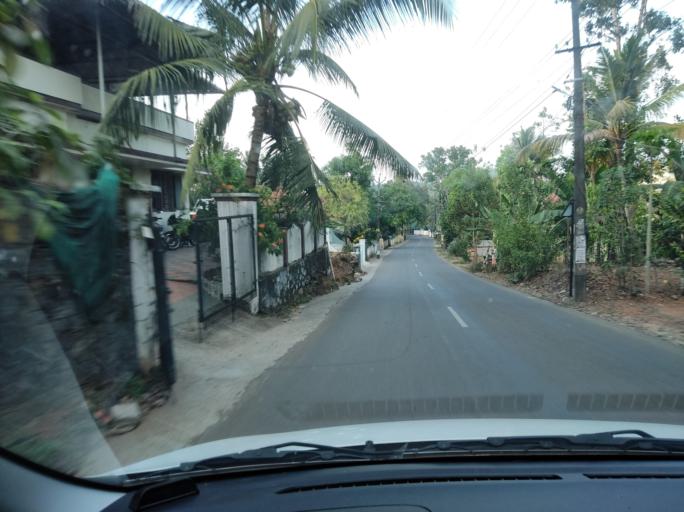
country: IN
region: Kerala
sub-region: Kottayam
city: Kottayam
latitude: 9.6431
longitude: 76.5092
